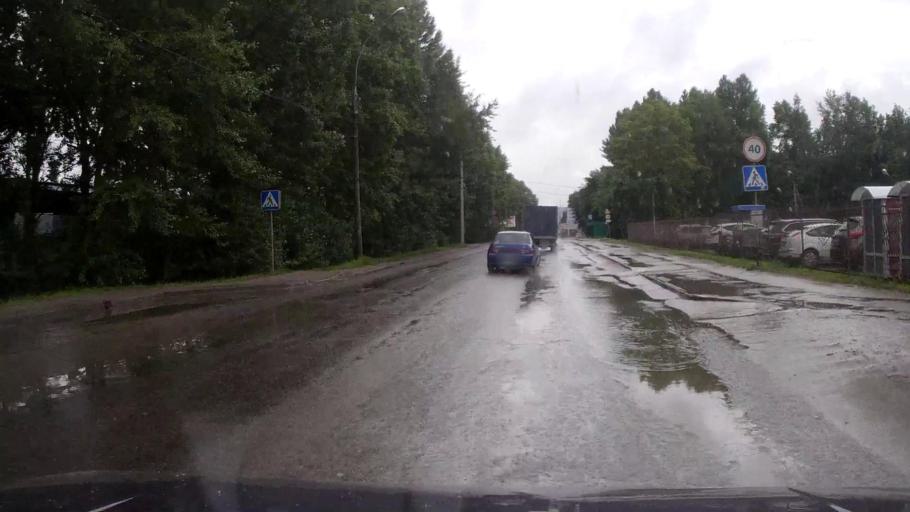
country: RU
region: Vologda
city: Vologda
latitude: 59.2104
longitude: 39.8554
